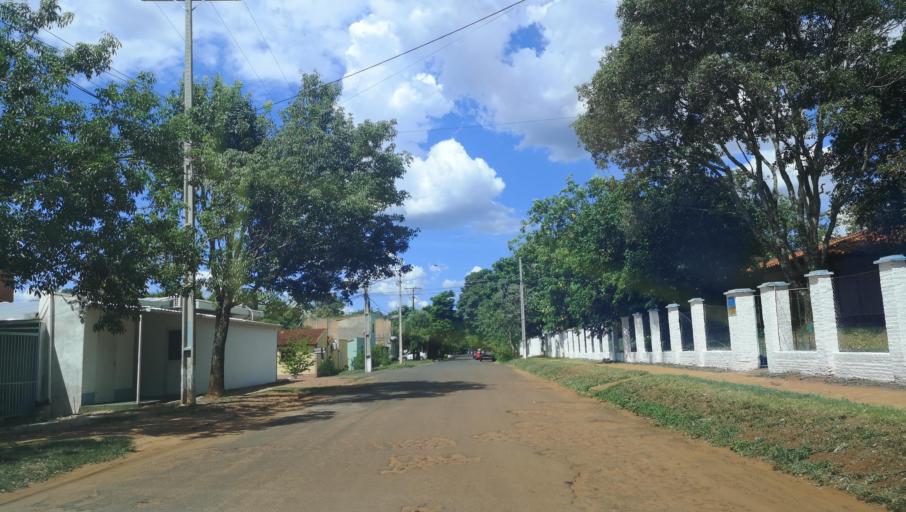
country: PY
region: Misiones
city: Santa Maria
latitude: -26.8916
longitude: -57.0349
